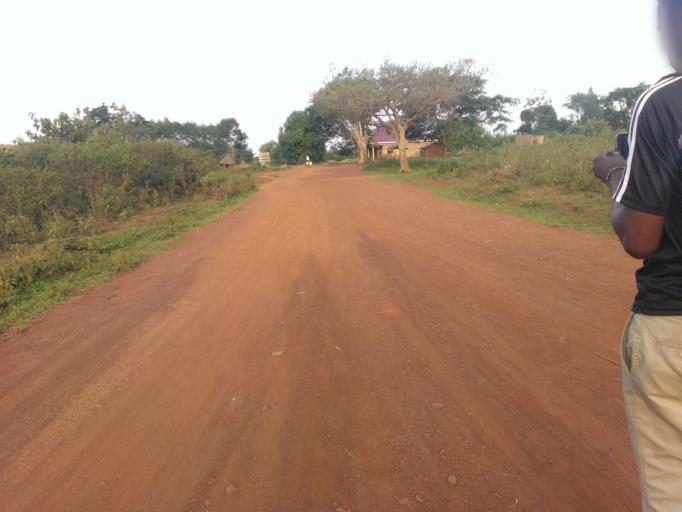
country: UG
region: Eastern Region
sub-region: Busia District
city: Busia
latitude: 0.5284
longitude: 34.0425
